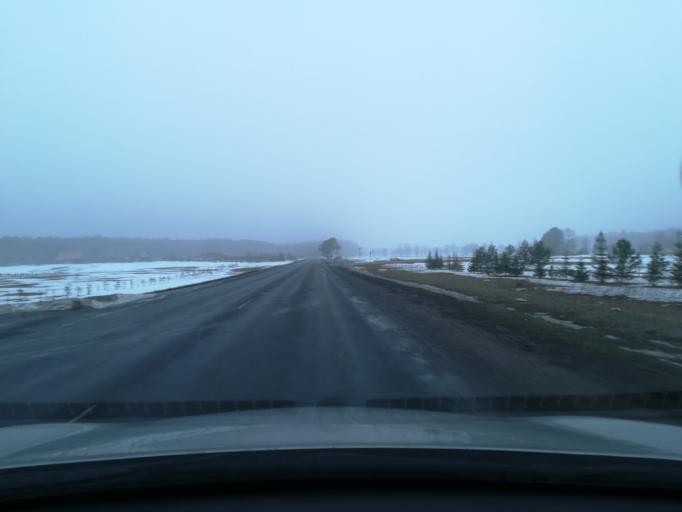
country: EE
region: Harju
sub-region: Raasiku vald
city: Arukula
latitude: 59.3521
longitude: 25.0834
